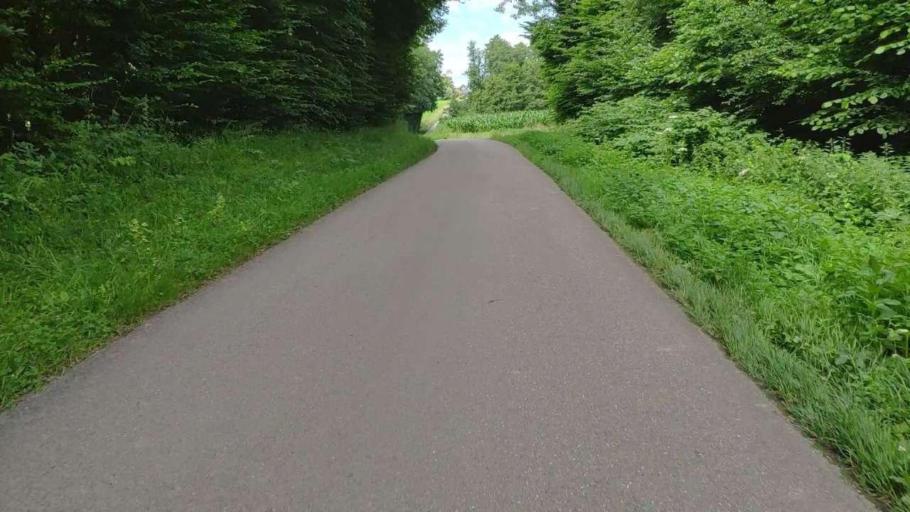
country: FR
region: Franche-Comte
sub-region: Departement du Jura
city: Chaussin
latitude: 46.8872
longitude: 5.4044
